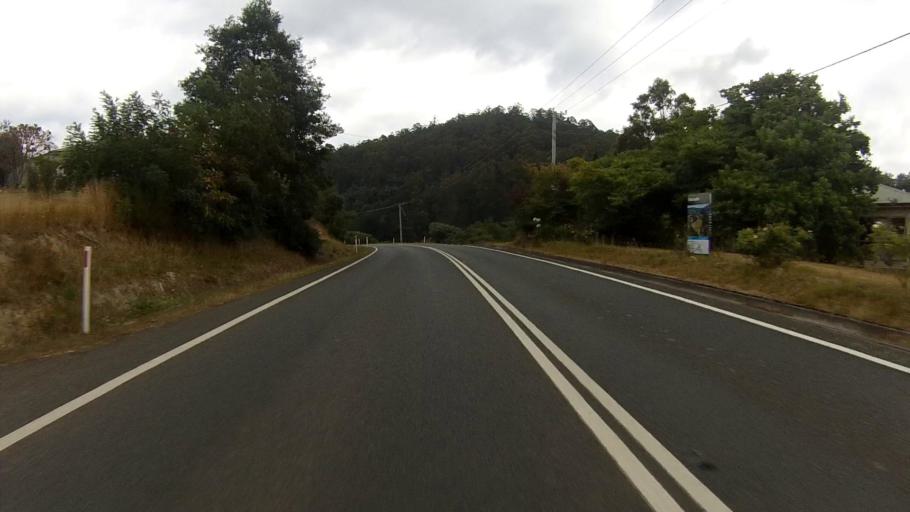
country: AU
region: Tasmania
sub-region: Huon Valley
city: Cygnet
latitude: -43.1424
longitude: 147.0639
